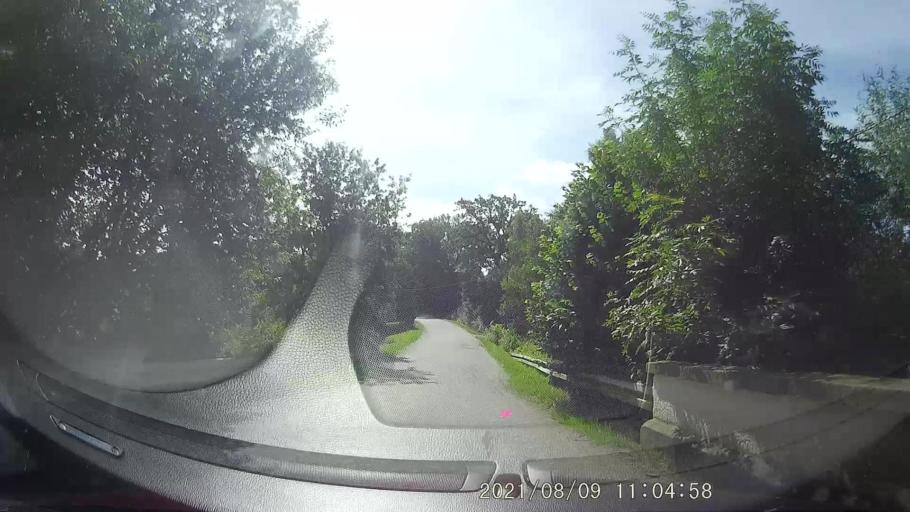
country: PL
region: Lower Silesian Voivodeship
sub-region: Powiat klodzki
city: Bozkow
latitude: 50.4615
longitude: 16.5754
